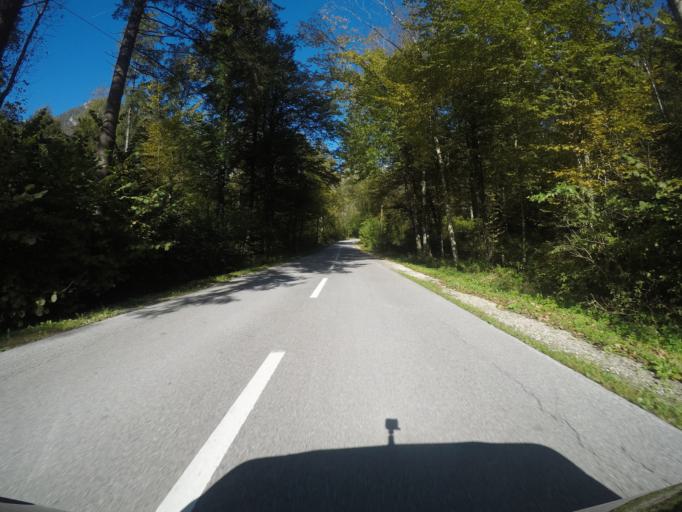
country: SI
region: Kamnik
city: Mekinje
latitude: 46.3135
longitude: 14.6047
